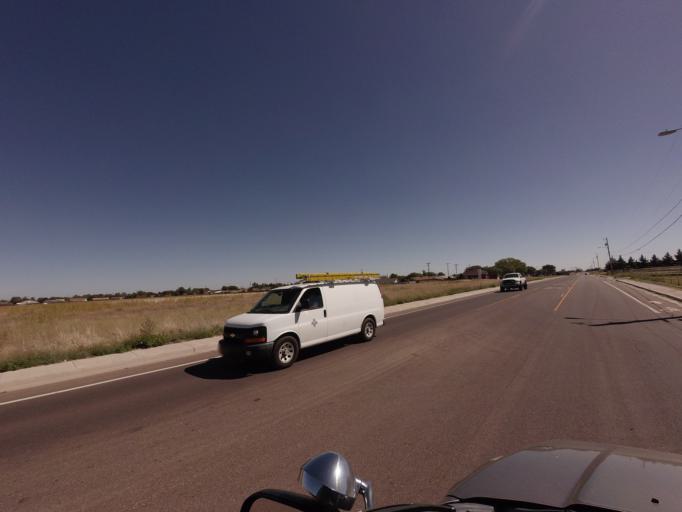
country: US
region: New Mexico
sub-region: Curry County
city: Clovis
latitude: 34.4314
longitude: -103.2318
